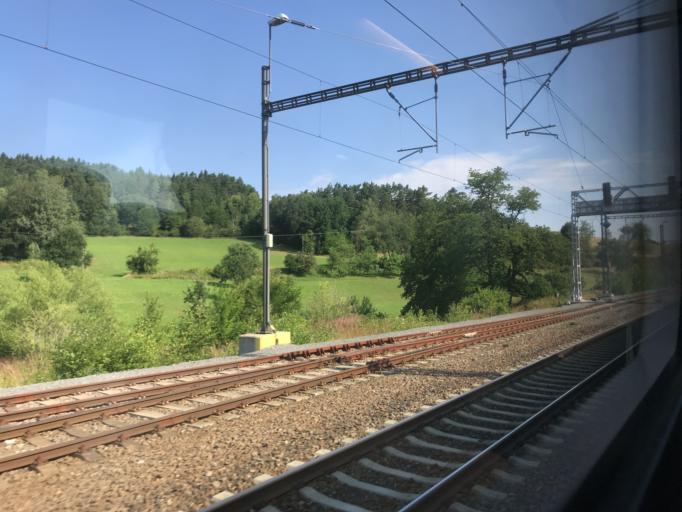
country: CZ
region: Central Bohemia
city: Votice
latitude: 49.6428
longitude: 14.6224
